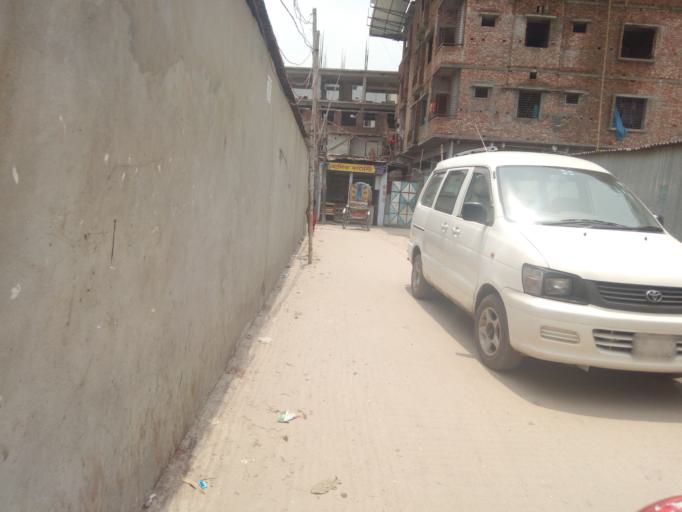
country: BD
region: Dhaka
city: Paltan
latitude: 23.7543
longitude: 90.4269
